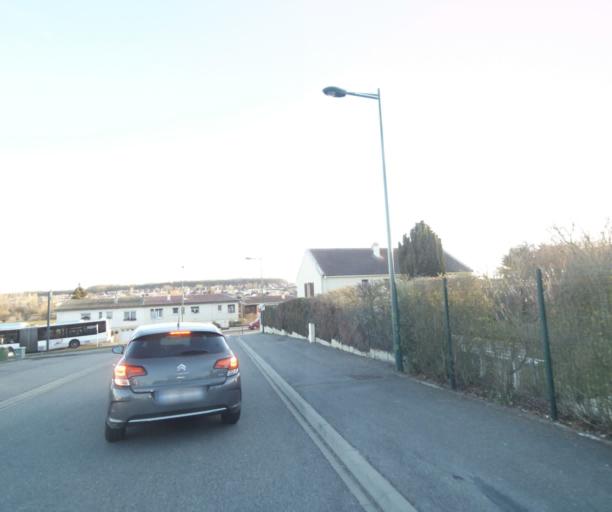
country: FR
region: Lorraine
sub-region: Departement de Meurthe-et-Moselle
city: Saulxures-les-Nancy
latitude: 48.6848
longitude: 6.2360
